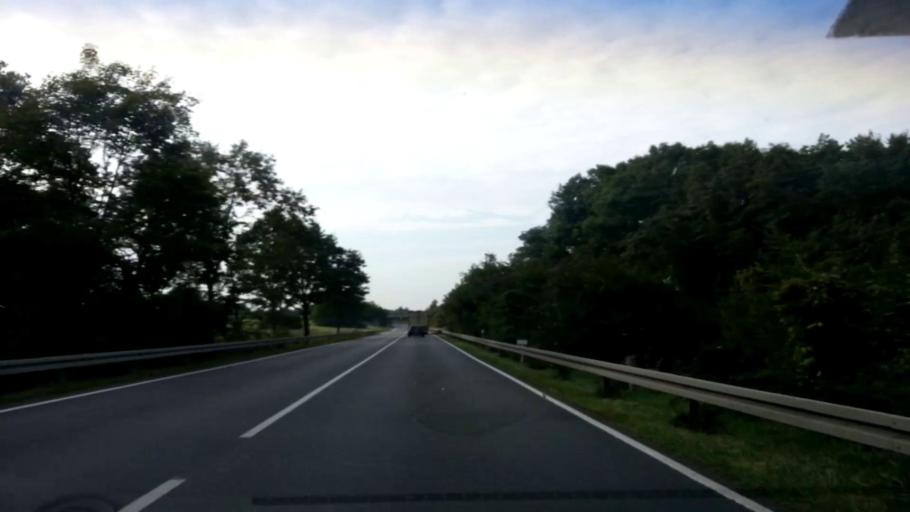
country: DE
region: Bavaria
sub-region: Regierungsbezirk Unterfranken
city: Wiesentheid
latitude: 49.8013
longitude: 10.3586
